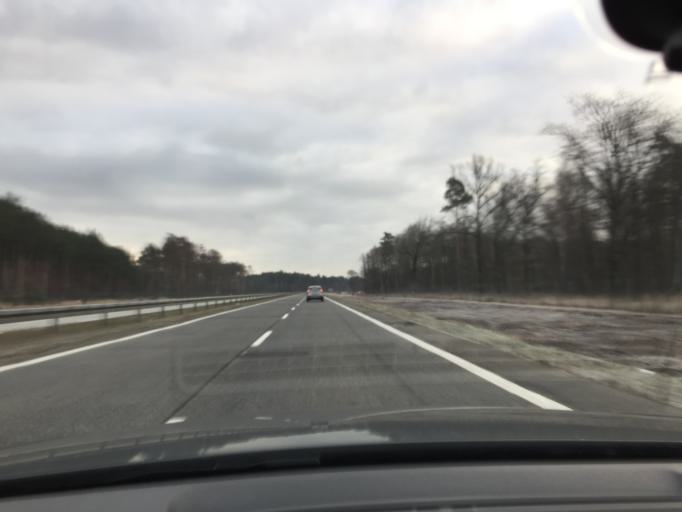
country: PL
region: Lubusz
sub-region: Powiat zarski
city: Lipinki Luzyckie
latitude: 51.6094
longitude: 14.9710
